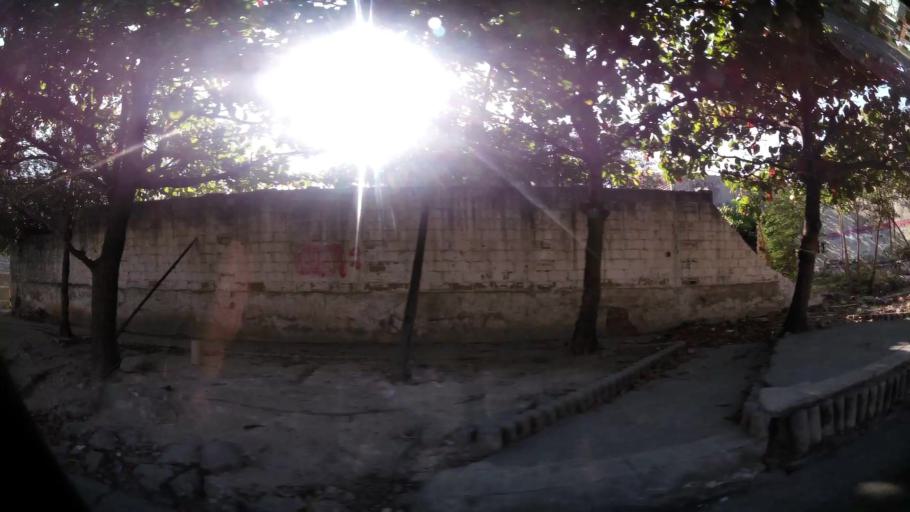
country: CO
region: Atlantico
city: Barranquilla
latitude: 11.0158
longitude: -74.7956
